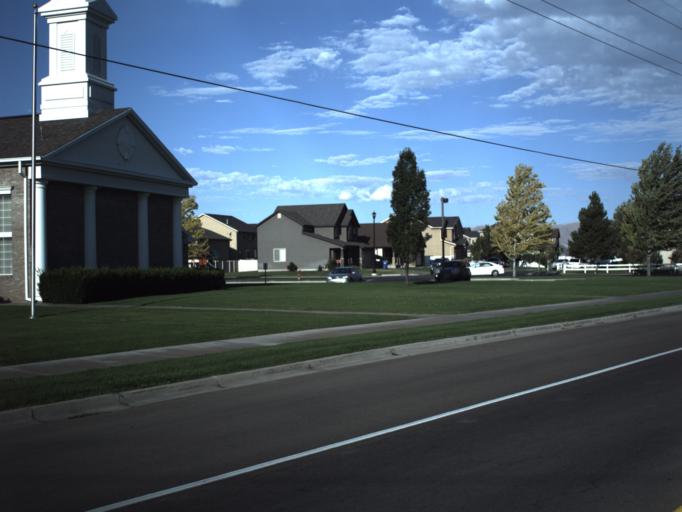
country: US
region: Utah
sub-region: Utah County
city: Spanish Fork
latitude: 40.0968
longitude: -111.6187
